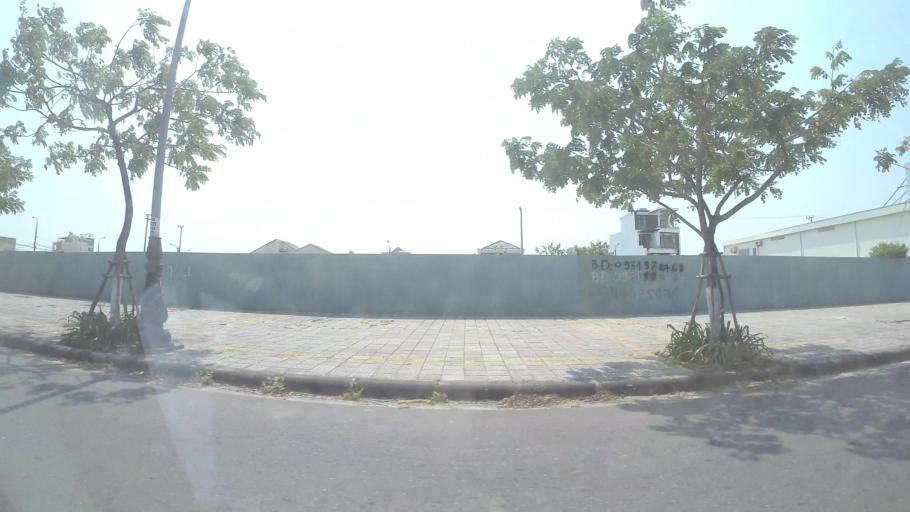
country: VN
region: Da Nang
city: Ngu Hanh Son
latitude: 15.9886
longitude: 108.2715
